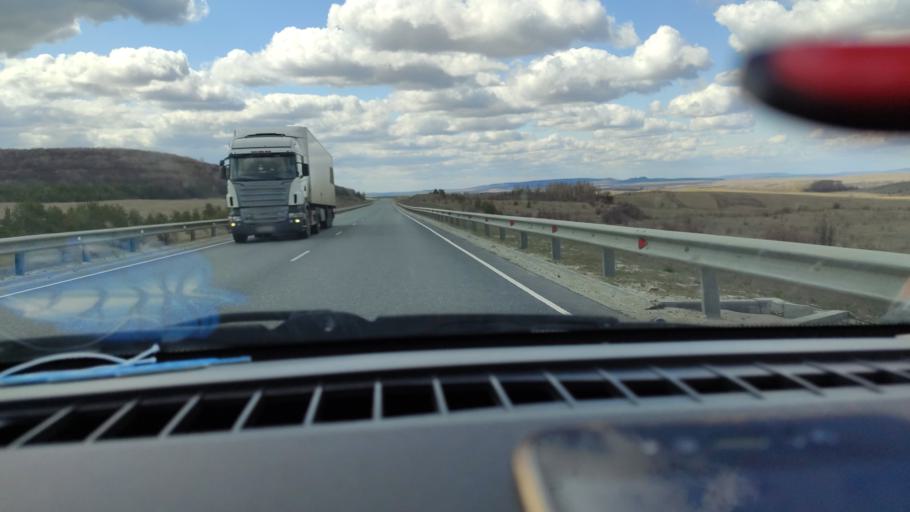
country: RU
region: Saratov
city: Alekseyevka
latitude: 52.3964
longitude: 47.9834
